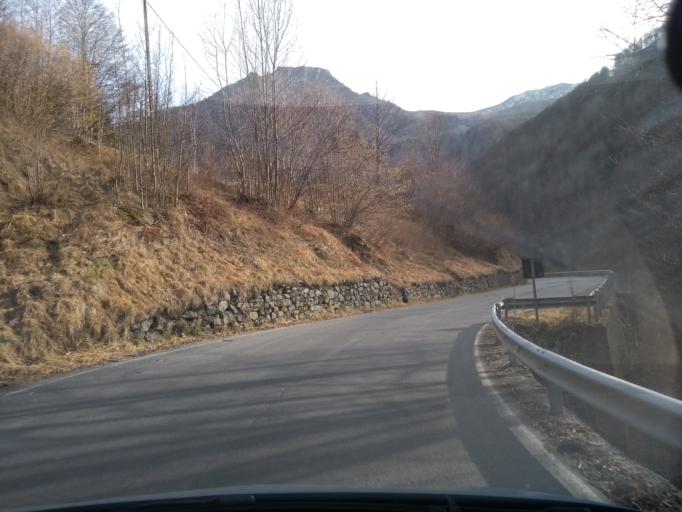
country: IT
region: Piedmont
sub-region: Provincia di Torino
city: Ala di Stura
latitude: 45.3133
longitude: 7.3155
